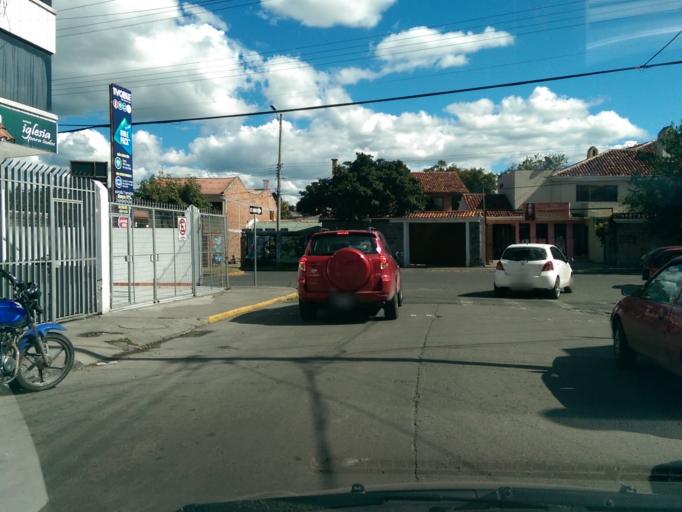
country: EC
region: Azuay
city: Cuenca
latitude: -2.8994
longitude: -79.0162
